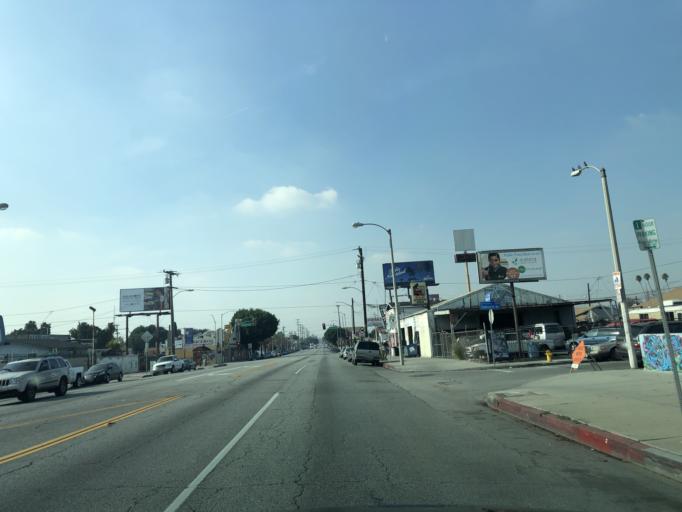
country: US
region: California
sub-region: Los Angeles County
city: East Los Angeles
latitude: 34.0190
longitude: -118.1880
